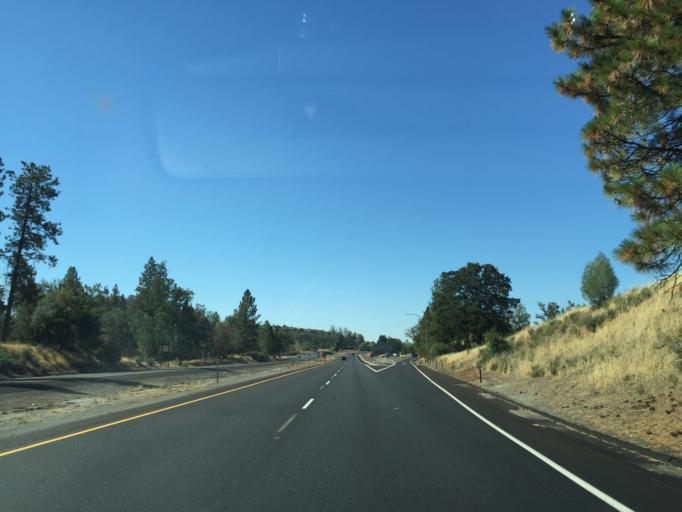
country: US
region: California
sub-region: Tuolumne County
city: Mono Vista
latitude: 37.9992
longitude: -120.2637
